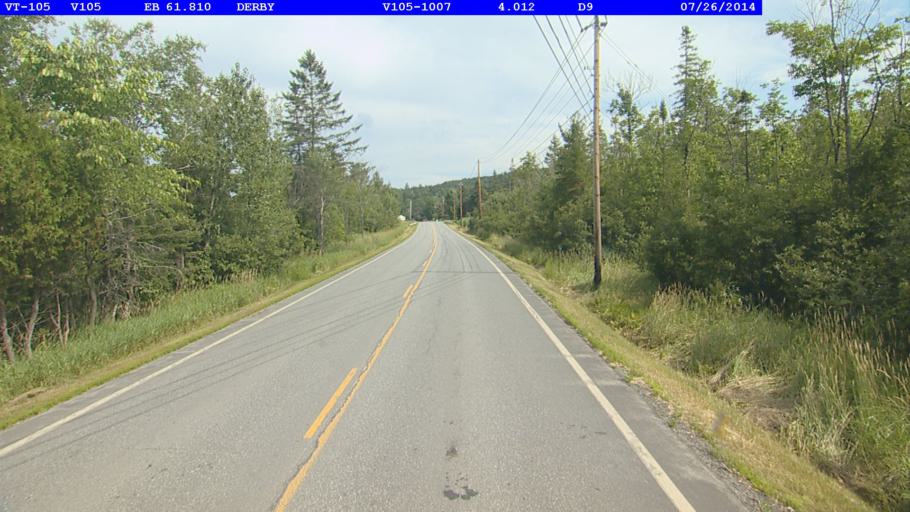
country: US
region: Vermont
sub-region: Orleans County
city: Newport
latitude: 44.9088
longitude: -72.0922
